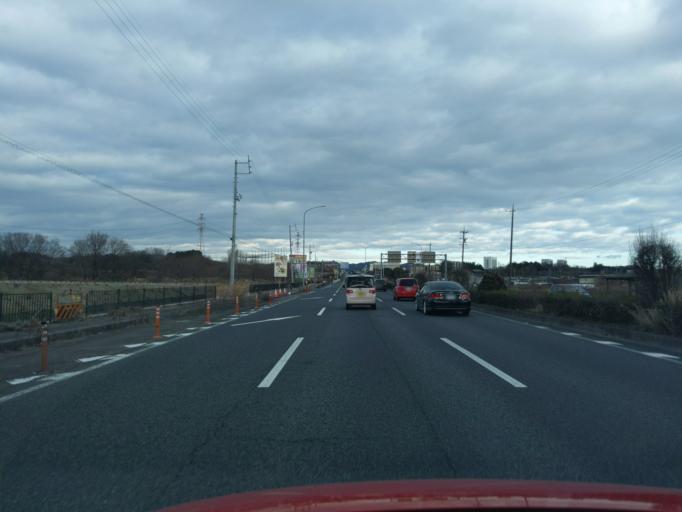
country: JP
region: Aichi
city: Kasugai
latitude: 35.2715
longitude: 137.0012
